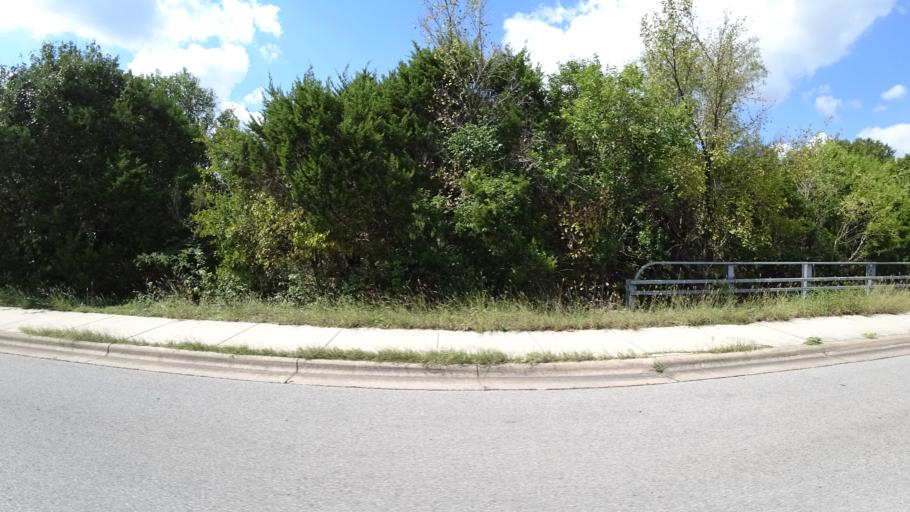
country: US
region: Texas
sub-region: Travis County
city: Onion Creek
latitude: 30.1880
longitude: -97.7906
